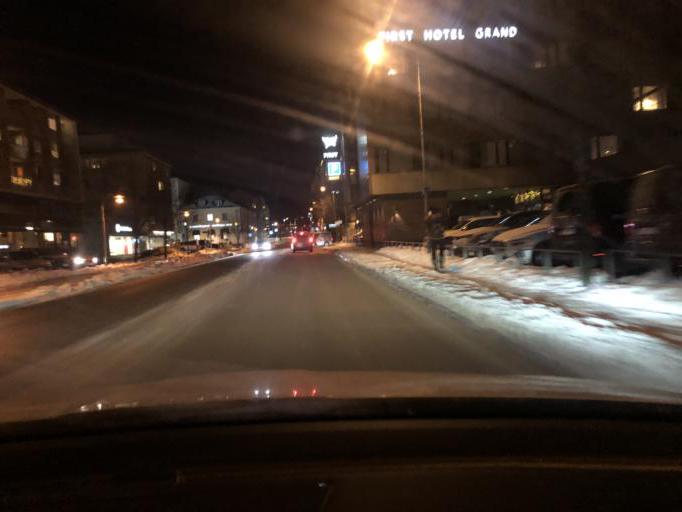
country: SE
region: Dalarna
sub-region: Faluns Kommun
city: Falun
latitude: 60.6069
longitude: 15.6337
